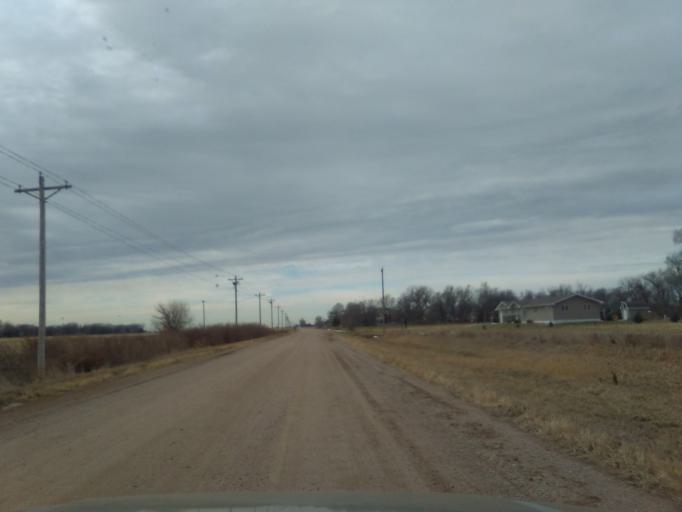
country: US
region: Nebraska
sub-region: Buffalo County
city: Gibbon
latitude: 40.6477
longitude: -98.8546
